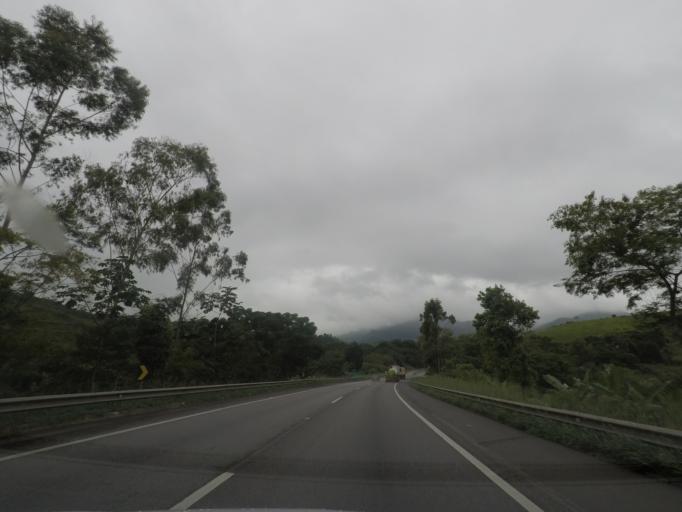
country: BR
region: Sao Paulo
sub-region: Cajati
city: Cajati
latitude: -24.7788
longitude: -48.1983
